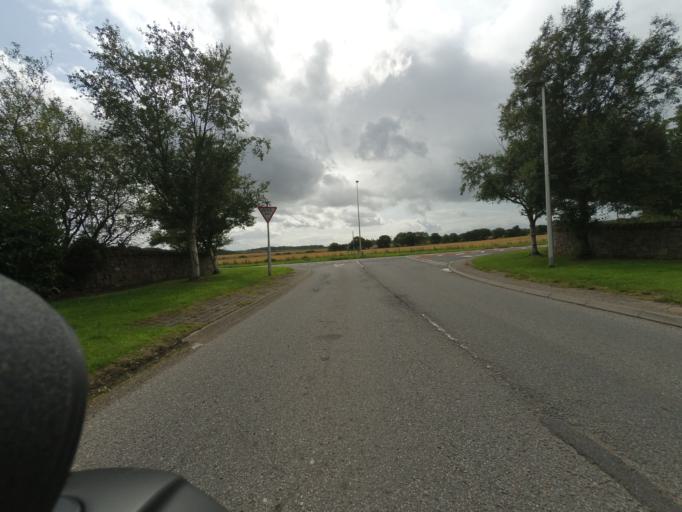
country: GB
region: Scotland
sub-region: Highland
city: Tain
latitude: 57.8026
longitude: -4.0455
